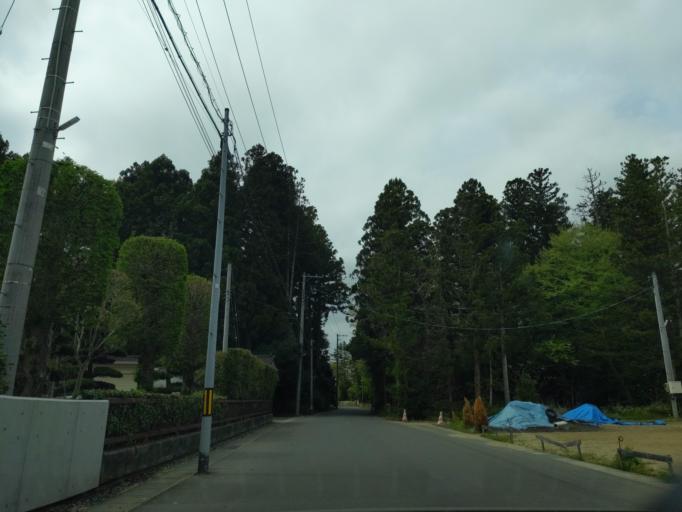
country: JP
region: Fukushima
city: Koriyama
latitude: 37.3805
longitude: 140.3097
